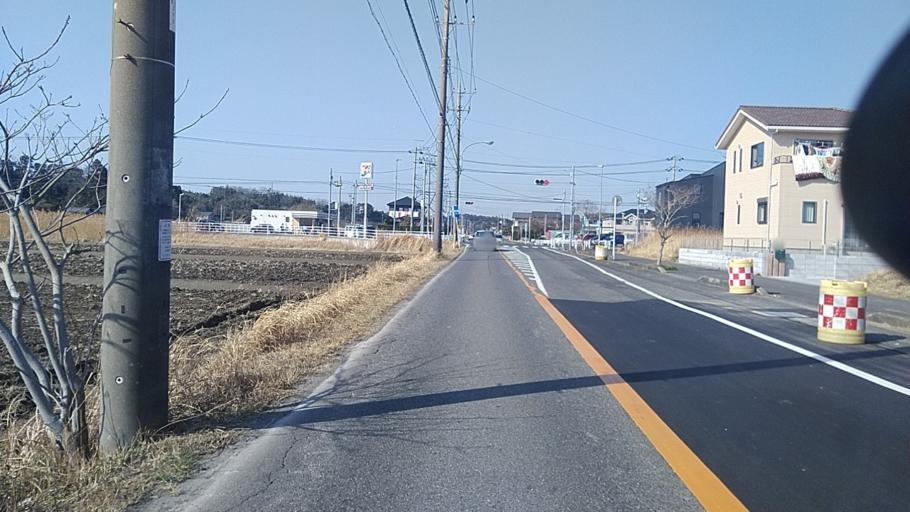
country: JP
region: Chiba
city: Mobara
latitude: 35.4533
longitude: 140.2905
